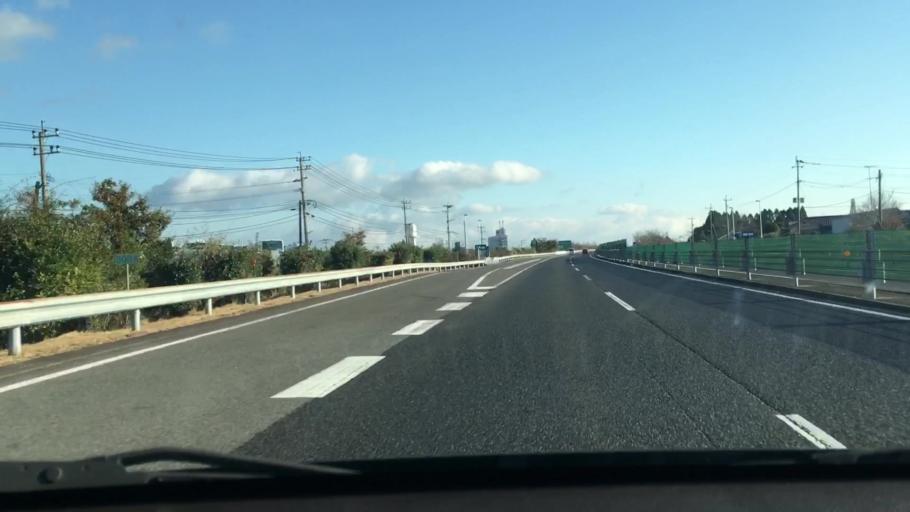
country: JP
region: Kagoshima
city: Kajiki
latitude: 31.8014
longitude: 130.7121
